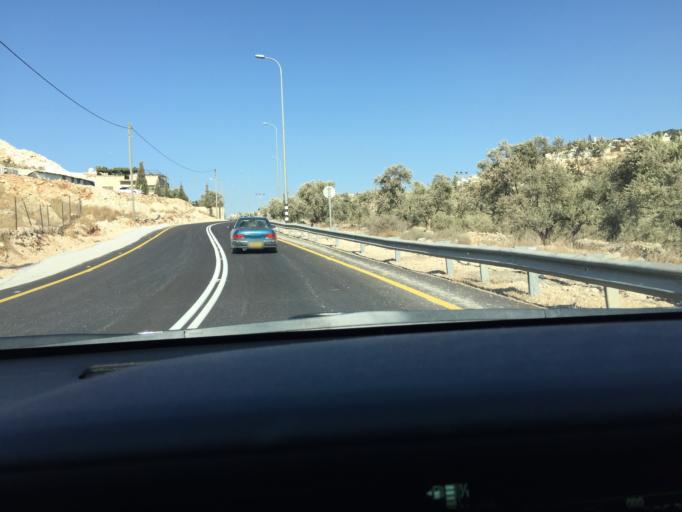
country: PS
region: West Bank
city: Rafat
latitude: 32.0639
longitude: 35.0420
